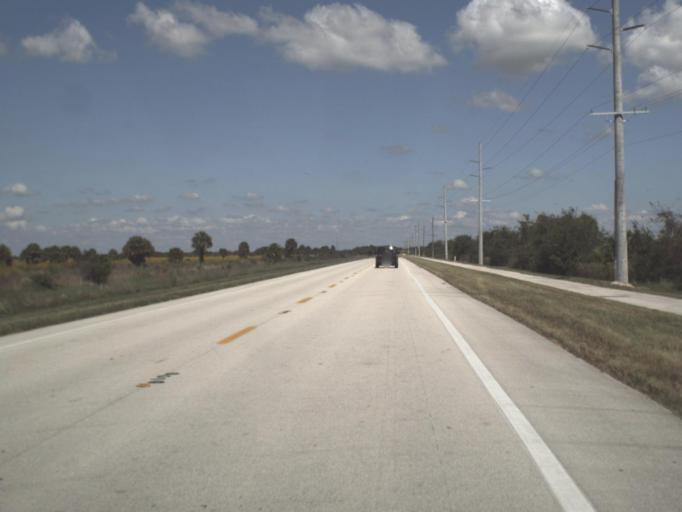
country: US
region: Florida
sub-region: Glades County
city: Moore Haven
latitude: 26.9443
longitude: -81.1222
